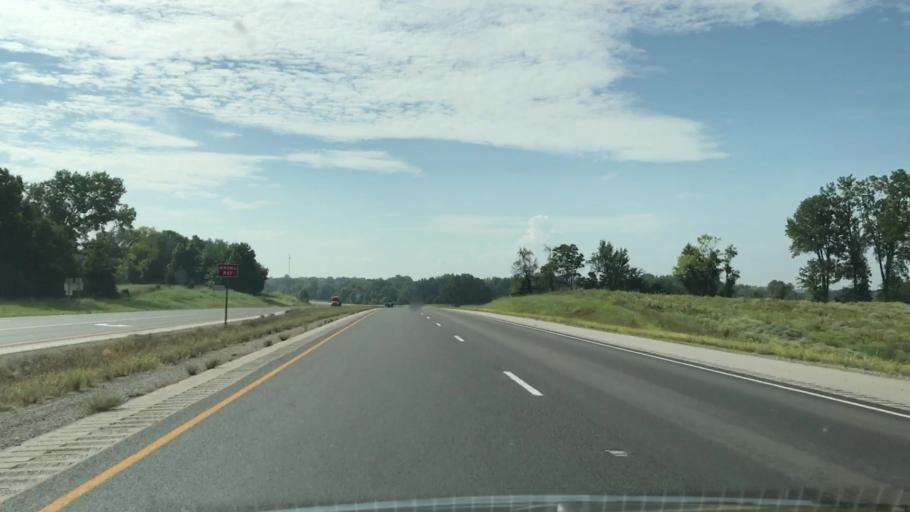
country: US
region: Kentucky
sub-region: Warren County
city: Plano
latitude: 36.8719
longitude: -86.3541
